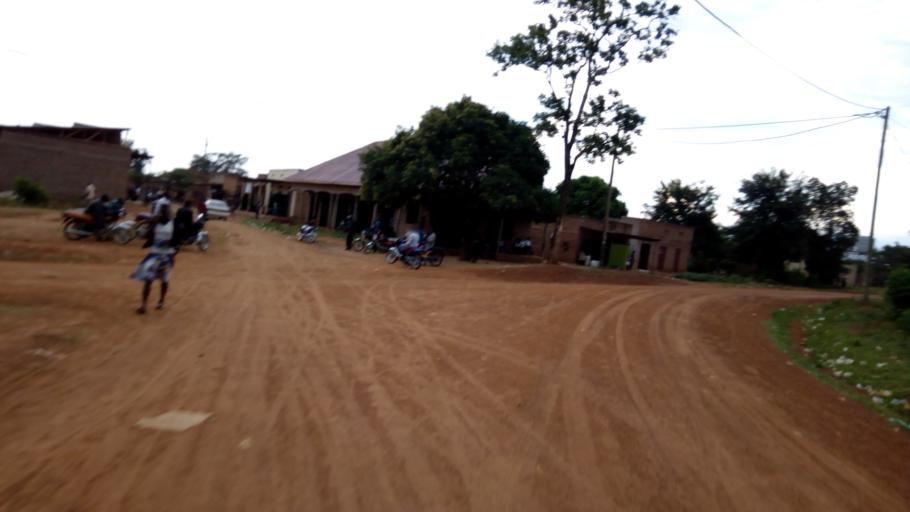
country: UG
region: Eastern Region
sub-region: Mbale District
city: Mbale
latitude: 1.1379
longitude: 34.1103
